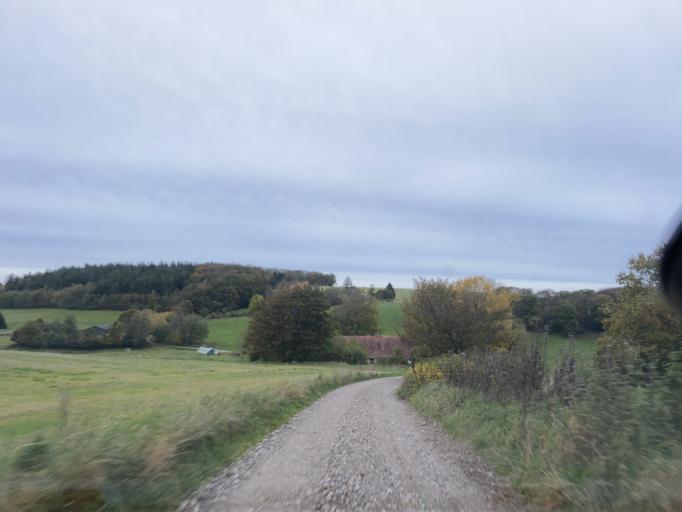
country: DK
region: Central Jutland
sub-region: Favrskov Kommune
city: Hammel
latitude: 56.1946
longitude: 9.7818
